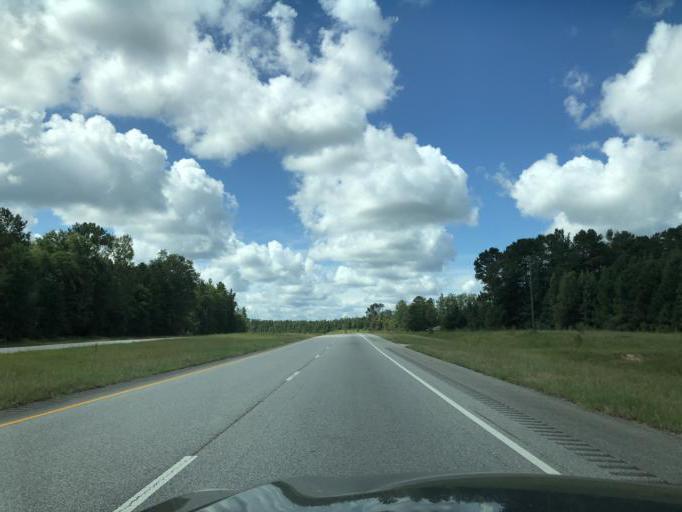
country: US
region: Alabama
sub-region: Russell County
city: Ladonia
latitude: 32.2387
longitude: -85.1691
